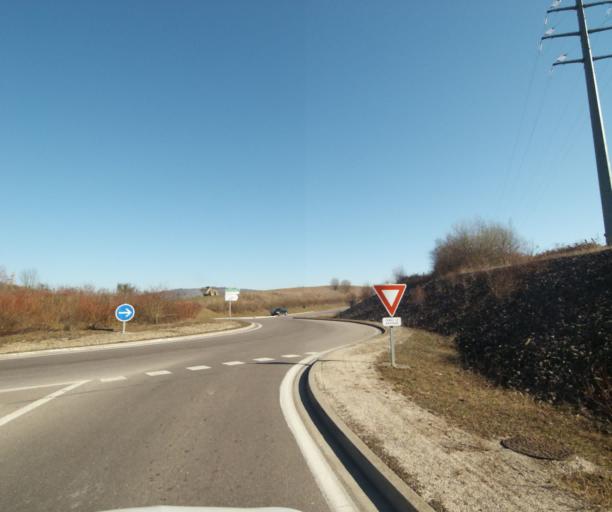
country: FR
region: Lorraine
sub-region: Departement de Meurthe-et-Moselle
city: Lay-Saint-Christophe
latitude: 48.7404
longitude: 6.1857
